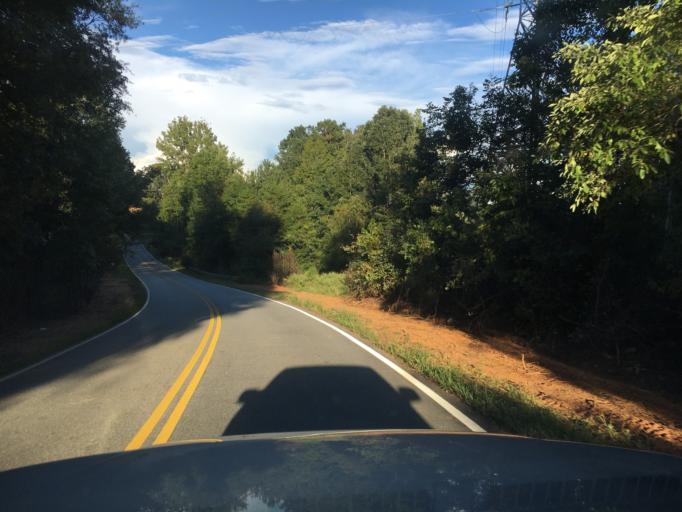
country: US
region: South Carolina
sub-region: Spartanburg County
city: Roebuck
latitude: 34.8859
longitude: -82.0012
